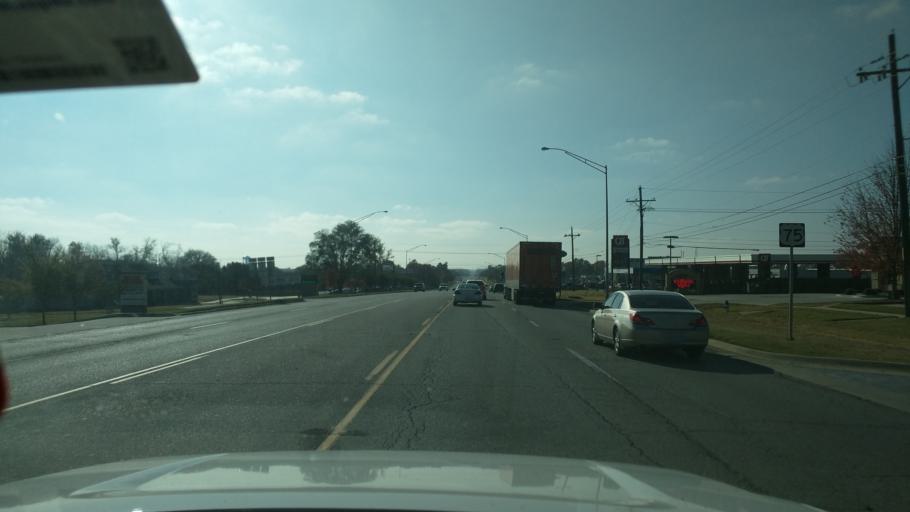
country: US
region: Oklahoma
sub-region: Washington County
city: Bartlesville
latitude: 36.7260
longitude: -95.9352
